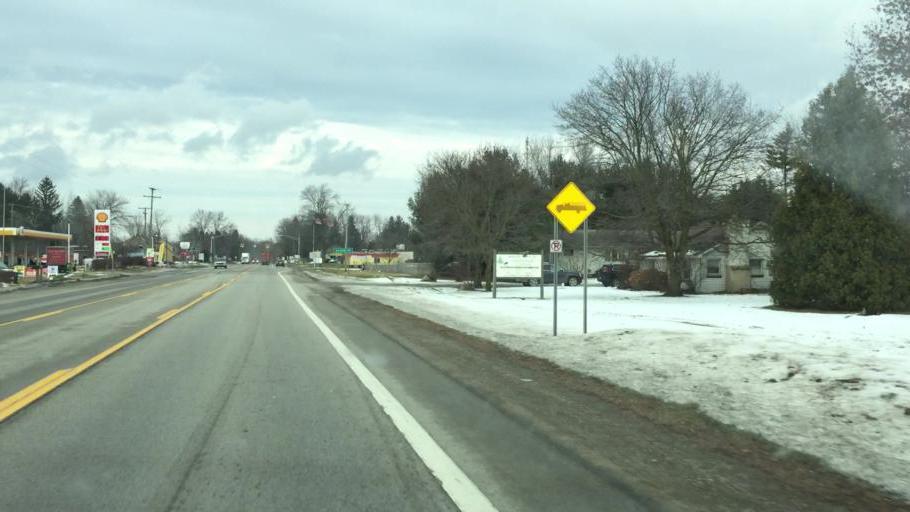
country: US
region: Michigan
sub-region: Lapeer County
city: Barnes Lake-Millers Lake
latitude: 43.2018
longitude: -83.3129
